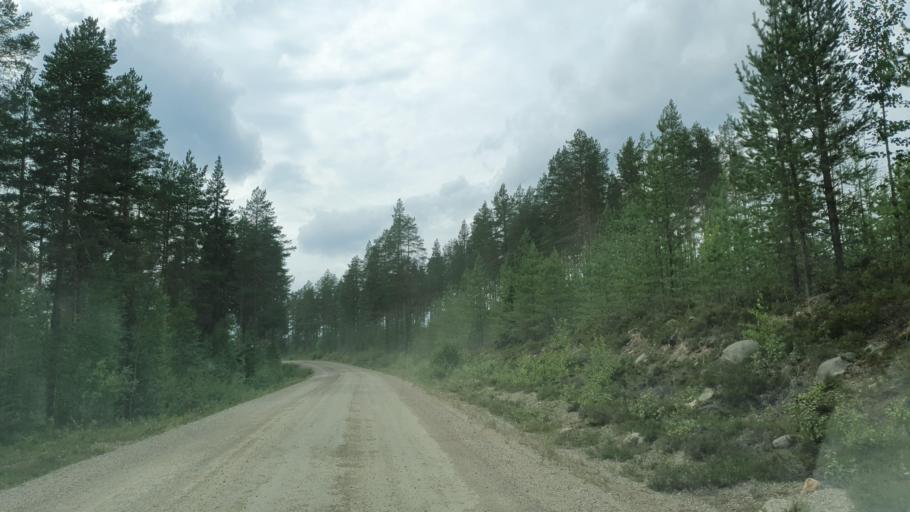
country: FI
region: Kainuu
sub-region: Kehys-Kainuu
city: Kuhmo
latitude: 64.7256
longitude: 29.7038
